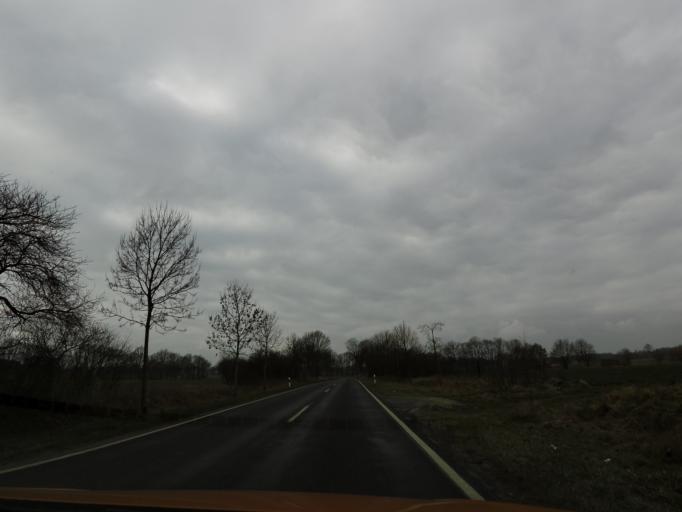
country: DE
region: Brandenburg
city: Ketzin
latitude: 52.4643
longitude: 12.9054
